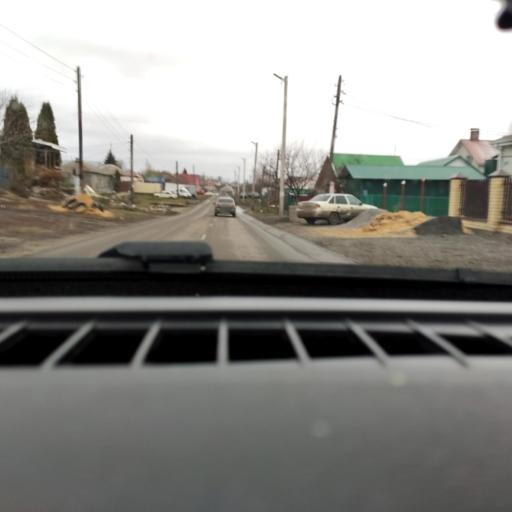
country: RU
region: Voronezj
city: Devitsa
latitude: 51.6381
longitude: 38.9356
